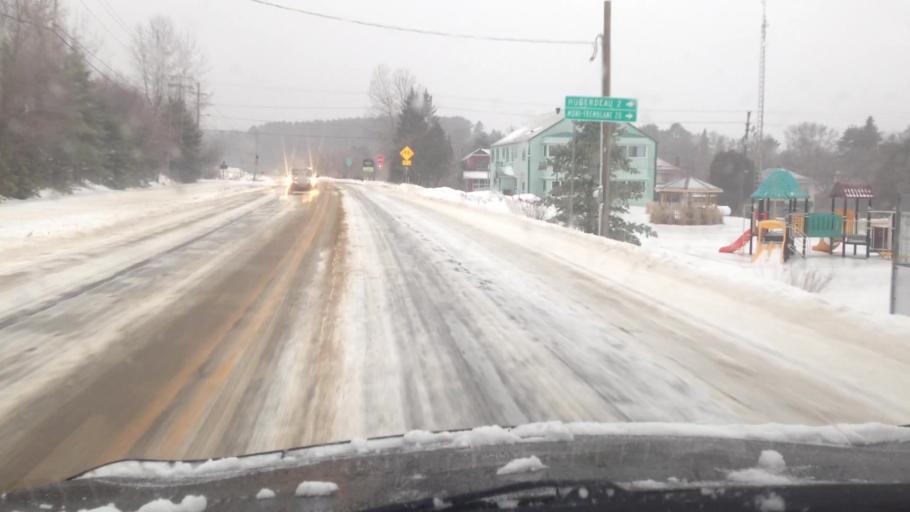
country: CA
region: Quebec
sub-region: Laurentides
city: Mont-Tremblant
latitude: 45.9660
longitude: -74.6150
